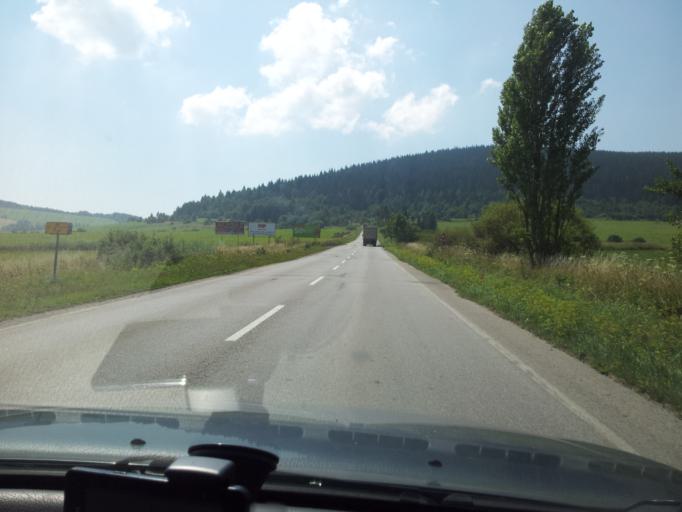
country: SK
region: Zilinsky
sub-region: Okres Dolny Kubin
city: Dolny Kubin
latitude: 49.3153
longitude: 19.3485
